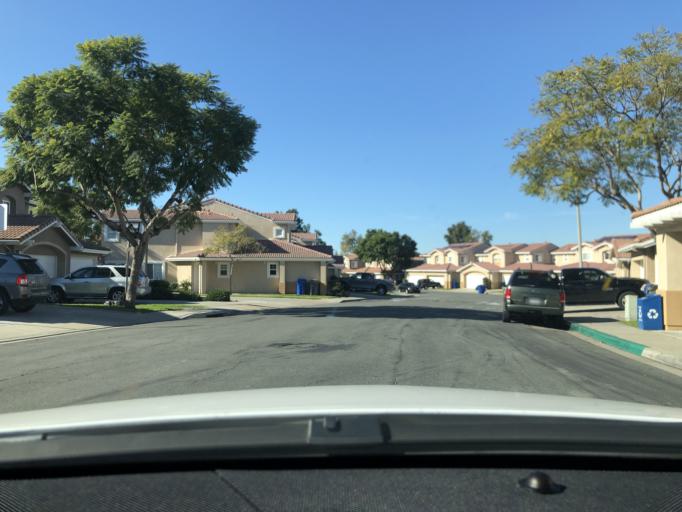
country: US
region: California
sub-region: San Diego County
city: Lemon Grove
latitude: 32.7407
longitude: -117.0650
